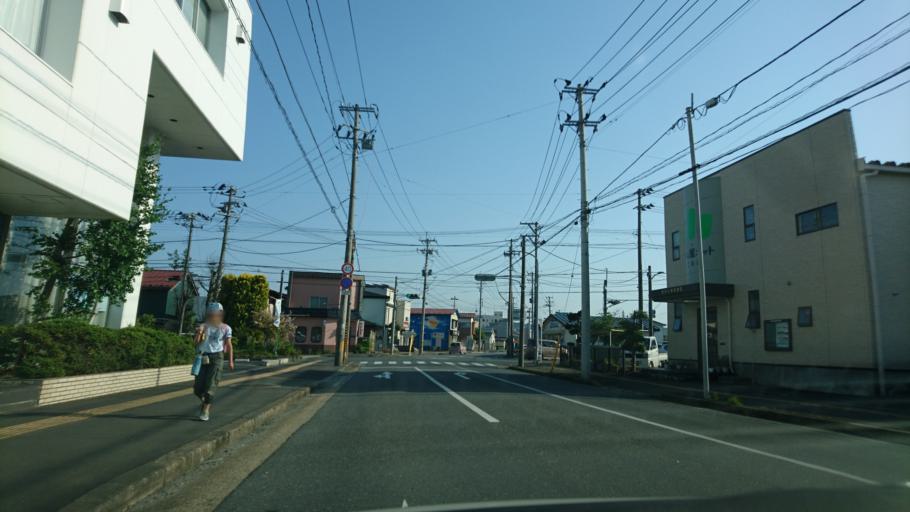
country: JP
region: Iwate
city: Ichinoseki
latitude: 38.9351
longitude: 141.1254
